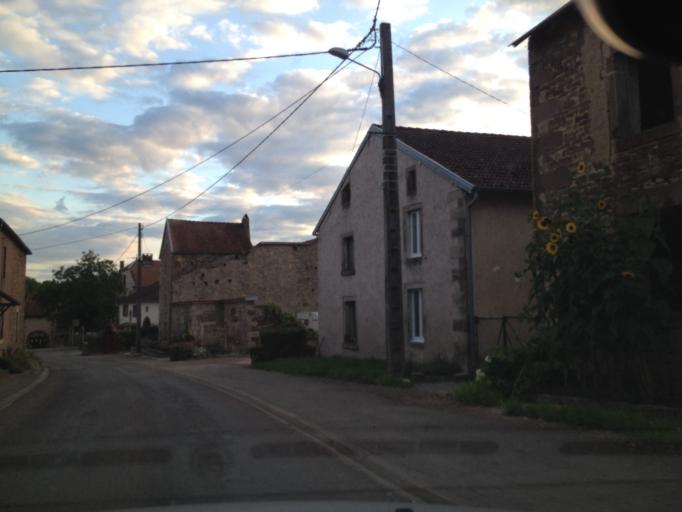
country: FR
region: Franche-Comte
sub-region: Departement de la Haute-Saone
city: Saint-Loup-sur-Semouse
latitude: 47.9329
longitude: 6.1656
